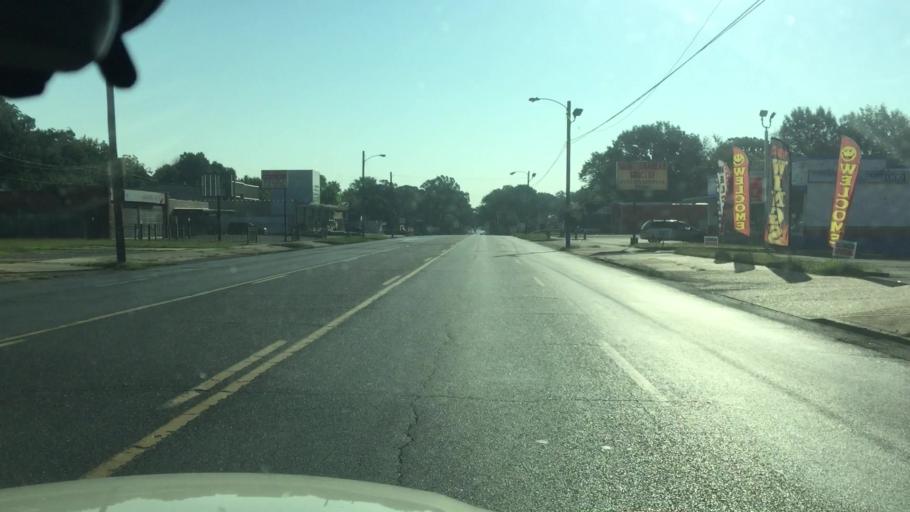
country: US
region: Tennessee
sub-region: Shelby County
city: Memphis
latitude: 35.1078
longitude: -89.9447
